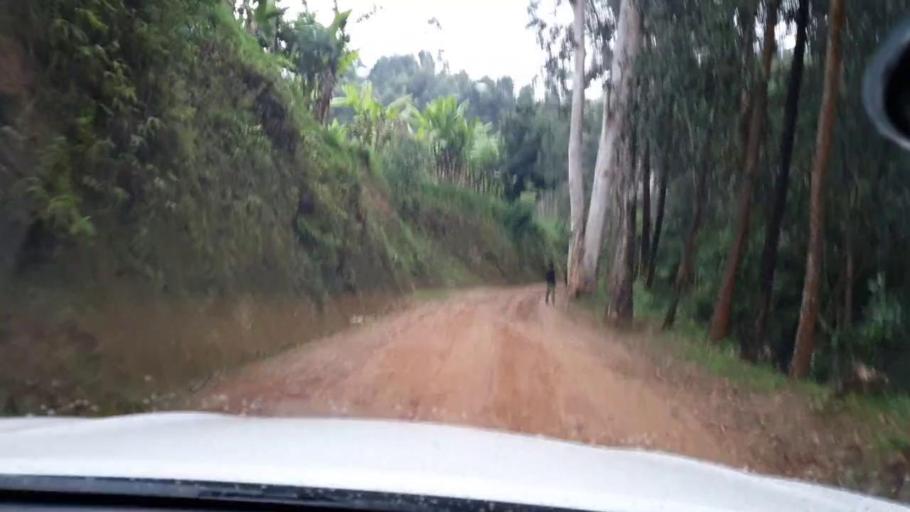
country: RW
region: Western Province
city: Cyangugu
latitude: -2.4103
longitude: 29.1884
